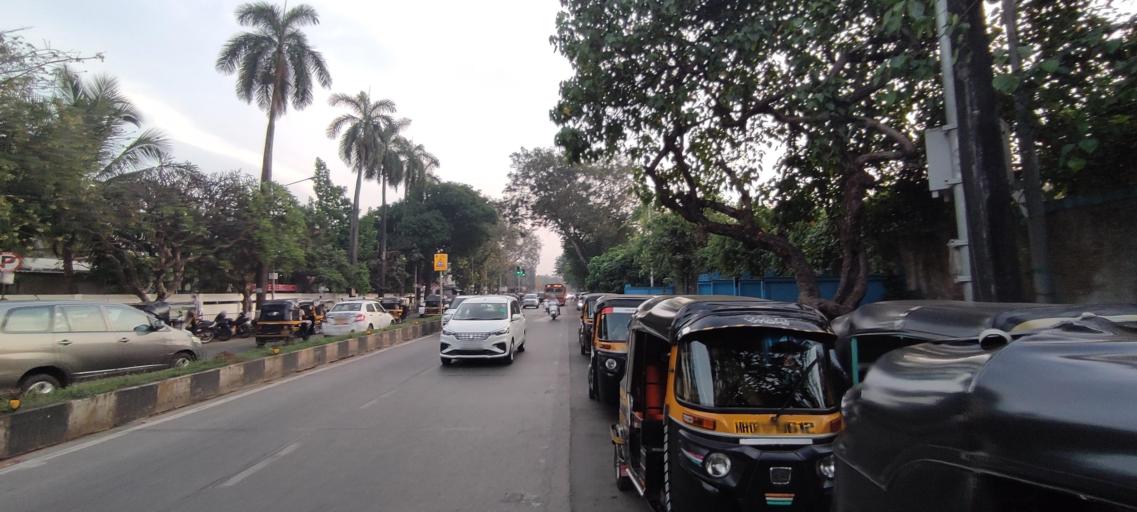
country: IN
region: Maharashtra
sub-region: Mumbai Suburban
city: Mumbai
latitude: 19.0963
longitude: 72.8395
